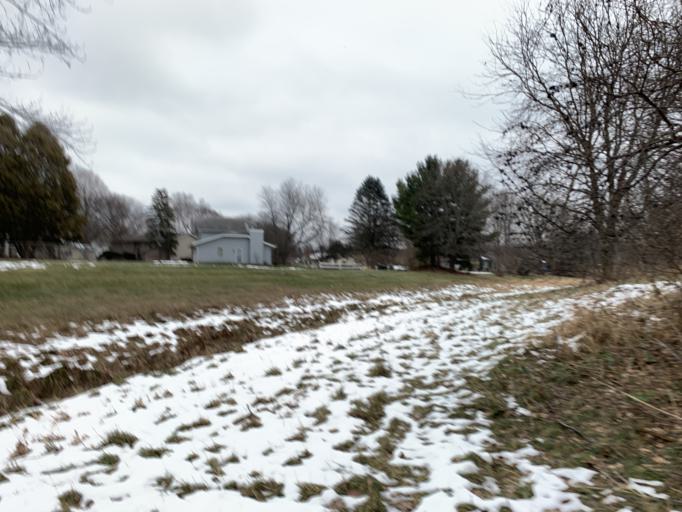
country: US
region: Wisconsin
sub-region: Dane County
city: Middleton
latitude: 43.0771
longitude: -89.5116
